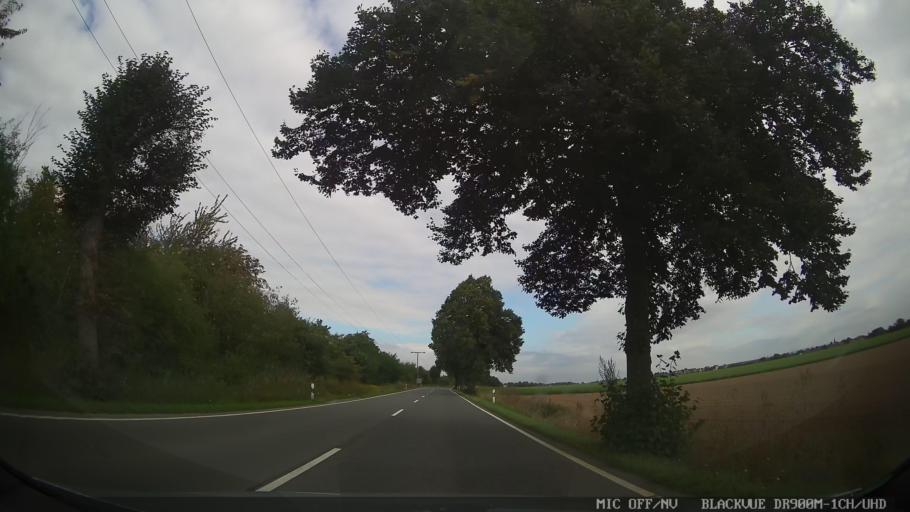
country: DE
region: Lower Saxony
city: Cramme
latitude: 52.1597
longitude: 10.4627
